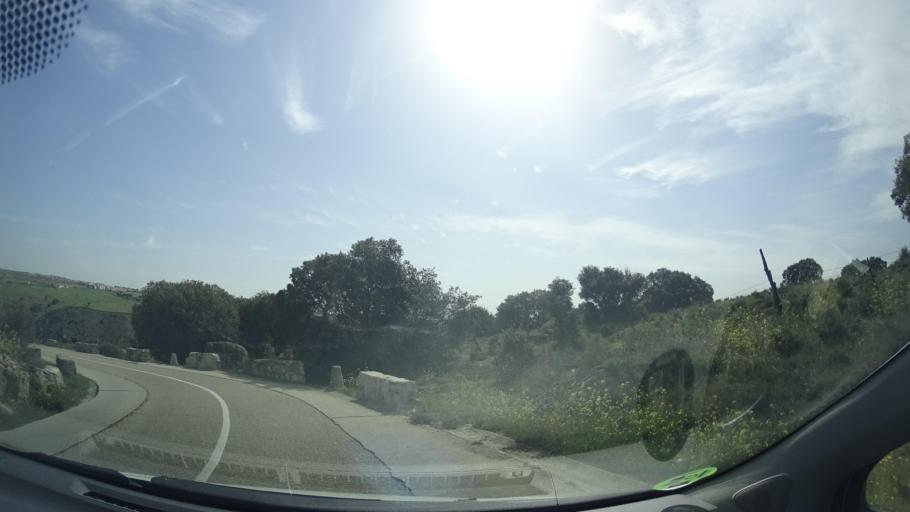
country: ES
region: Madrid
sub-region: Provincia de Madrid
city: Colmenar Viejo
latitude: 40.6422
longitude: -3.8127
